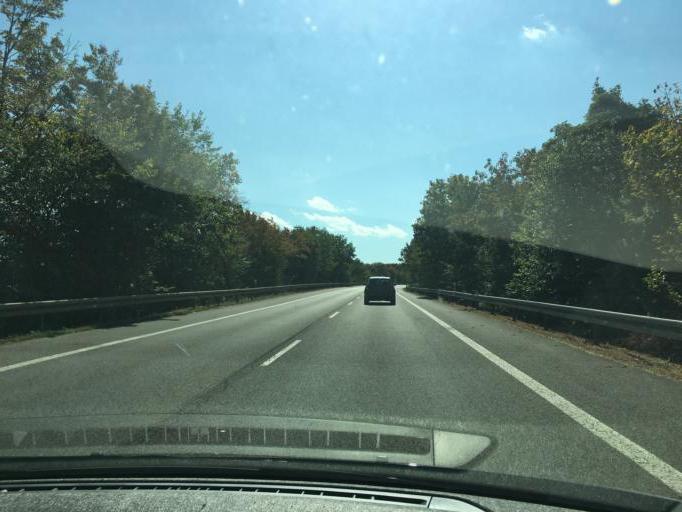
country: DE
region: North Rhine-Westphalia
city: Zulpich
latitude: 50.6872
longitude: 6.6353
